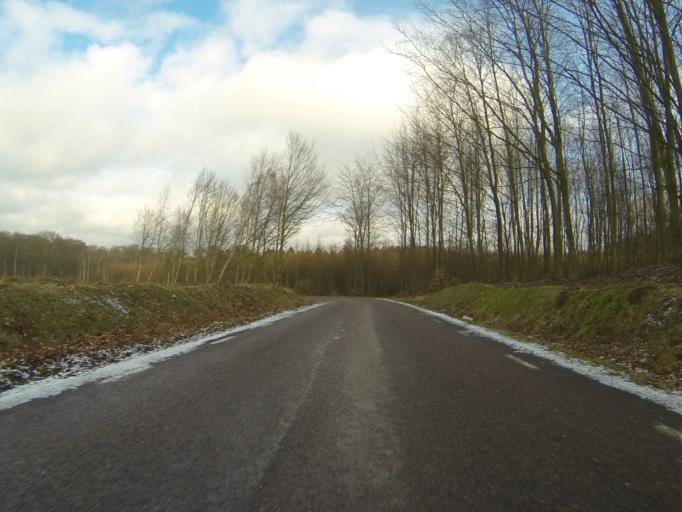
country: SE
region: Skane
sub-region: Svedala Kommun
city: Svedala
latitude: 55.5333
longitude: 13.2770
